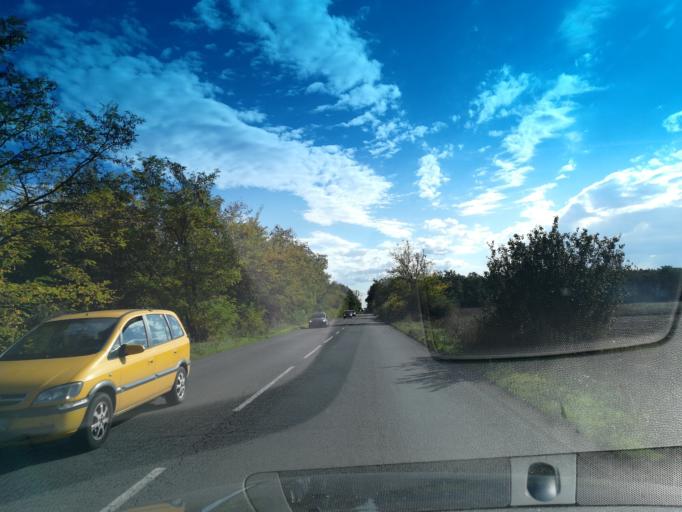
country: BG
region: Stara Zagora
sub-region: Obshtina Stara Zagora
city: Stara Zagora
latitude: 42.3553
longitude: 25.6574
